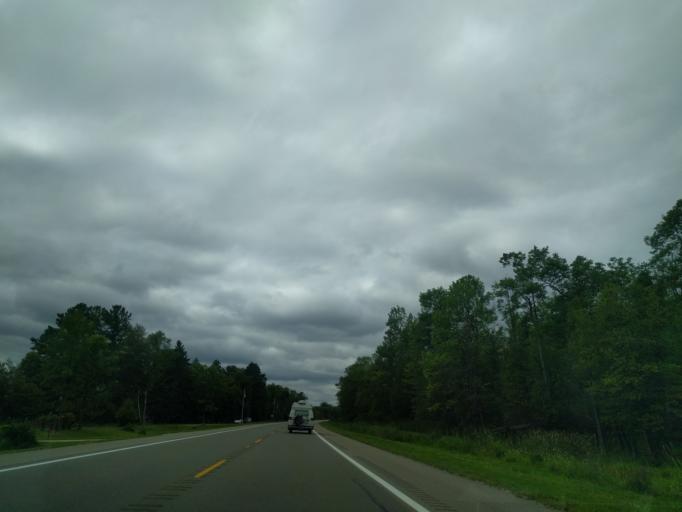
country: US
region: Michigan
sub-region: Menominee County
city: Menominee
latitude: 45.2201
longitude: -87.5169
